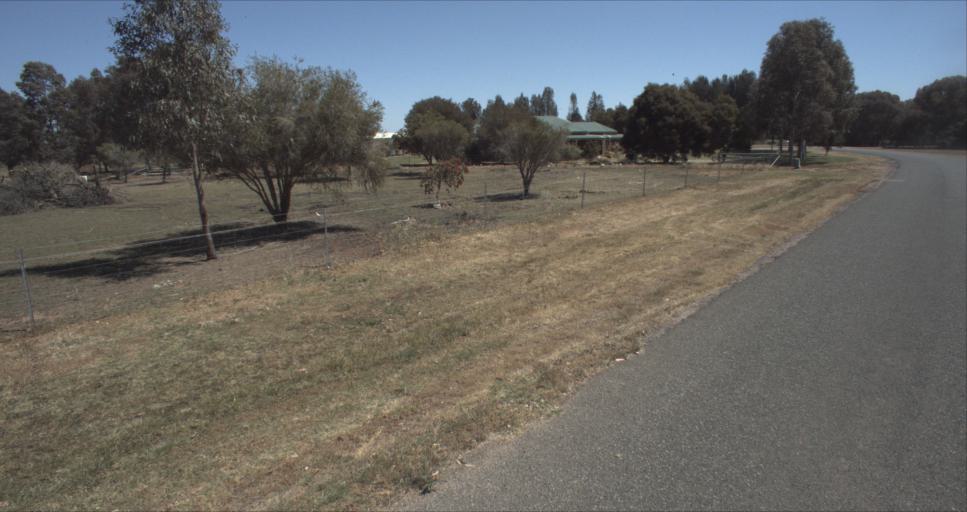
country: AU
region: New South Wales
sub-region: Leeton
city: Leeton
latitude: -34.5246
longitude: 146.4094
